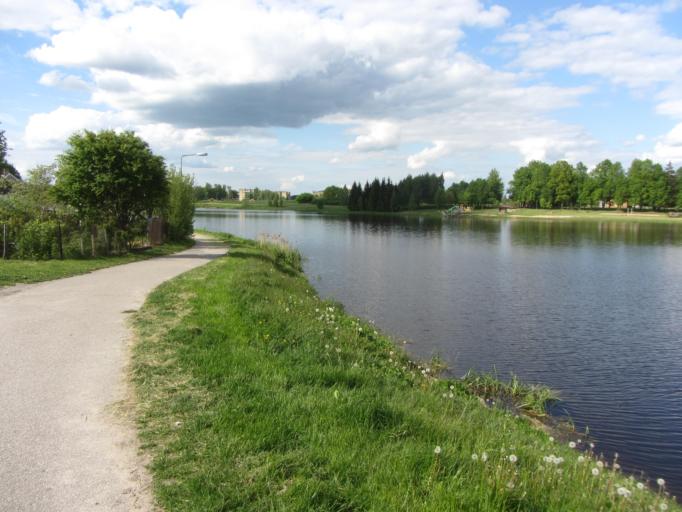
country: LT
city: Sirvintos
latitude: 55.0413
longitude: 24.9584
